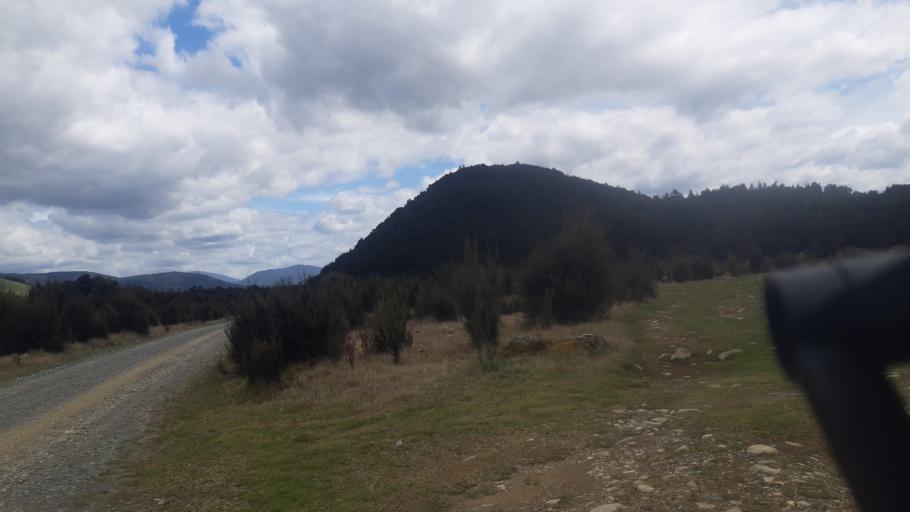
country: NZ
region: Tasman
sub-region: Tasman District
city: Wakefield
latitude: -41.7853
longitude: 172.8192
